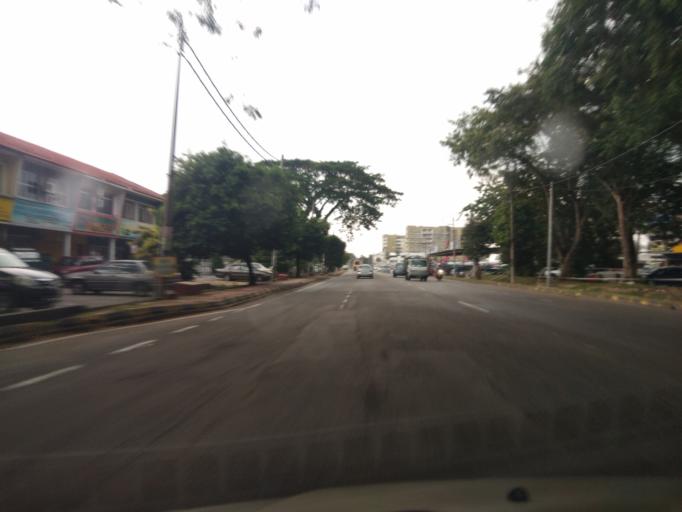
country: MY
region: Penang
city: Permatang Kuching
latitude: 5.4378
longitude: 100.3808
